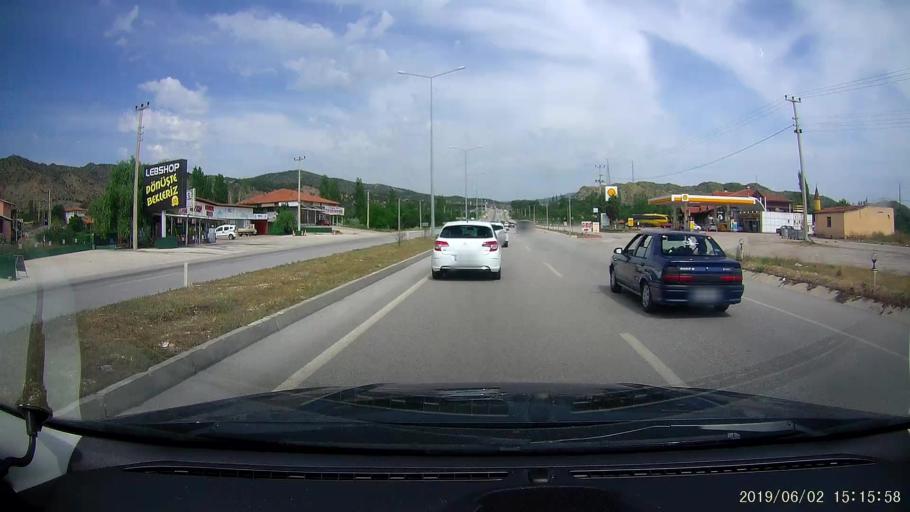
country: TR
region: Corum
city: Osmancik
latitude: 40.9703
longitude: 34.8575
